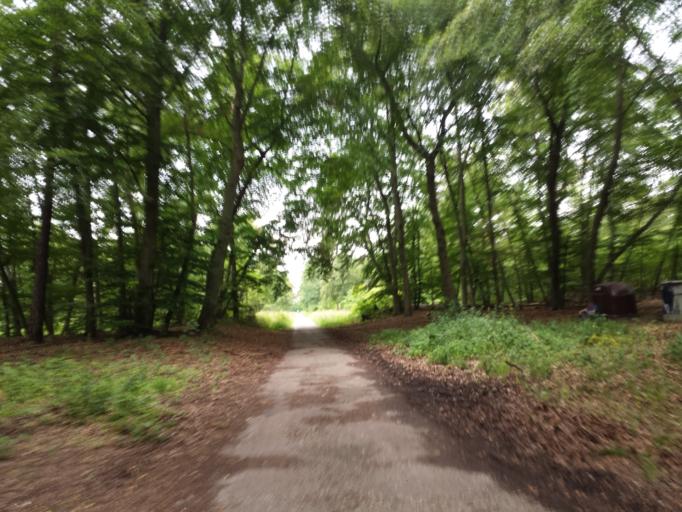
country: DE
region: Hesse
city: Viernheim
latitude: 49.5208
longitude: 8.5423
